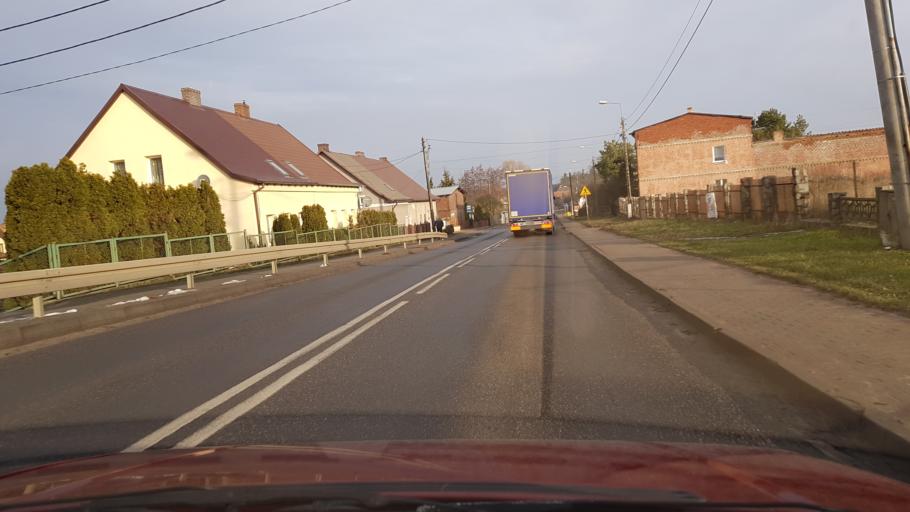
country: PL
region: West Pomeranian Voivodeship
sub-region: Powiat policki
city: Police
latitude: 53.5150
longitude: 14.5673
